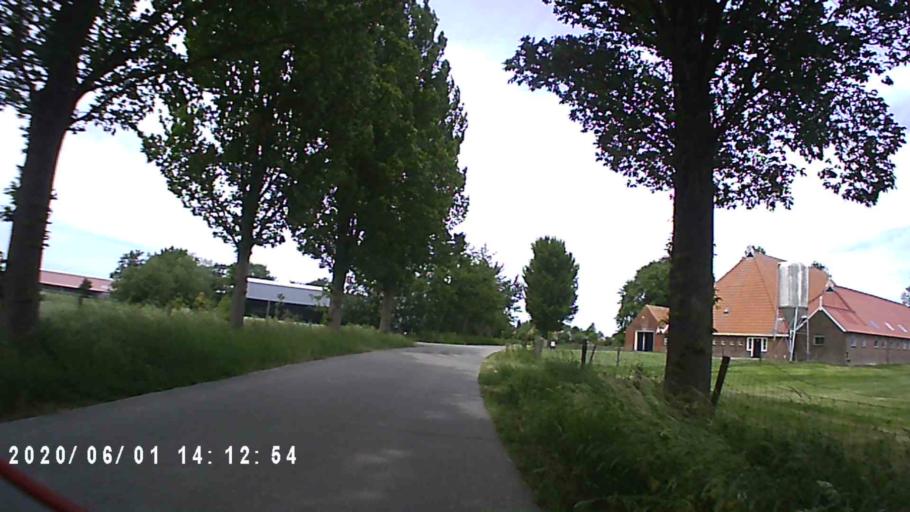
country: NL
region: Friesland
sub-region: Gemeente Littenseradiel
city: Winsum
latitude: 53.1311
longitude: 5.6504
